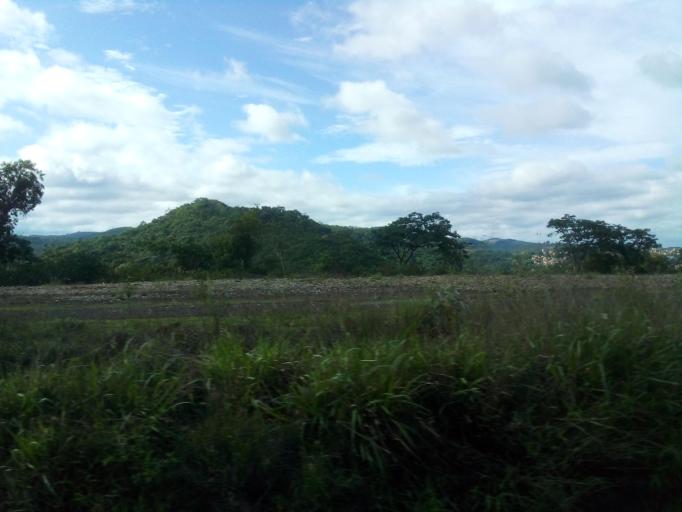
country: BR
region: Minas Gerais
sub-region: Raposos
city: Raposos
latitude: -19.8728
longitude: -43.7917
